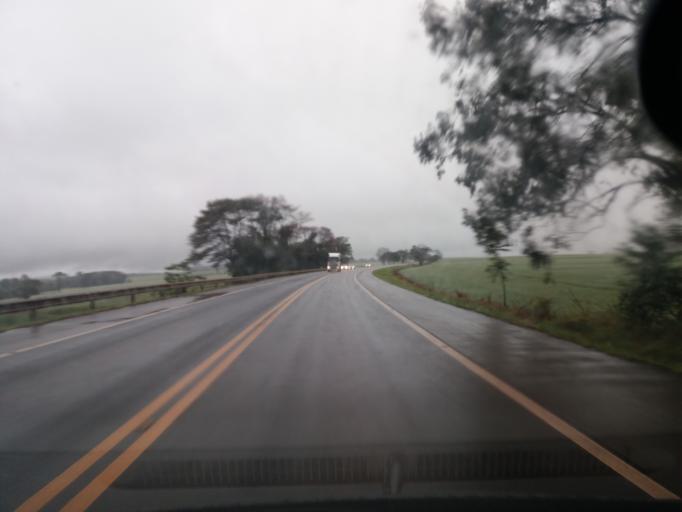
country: BR
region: Parana
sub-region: Campo Mourao
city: Campo Mourao
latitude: -24.3063
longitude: -52.6070
